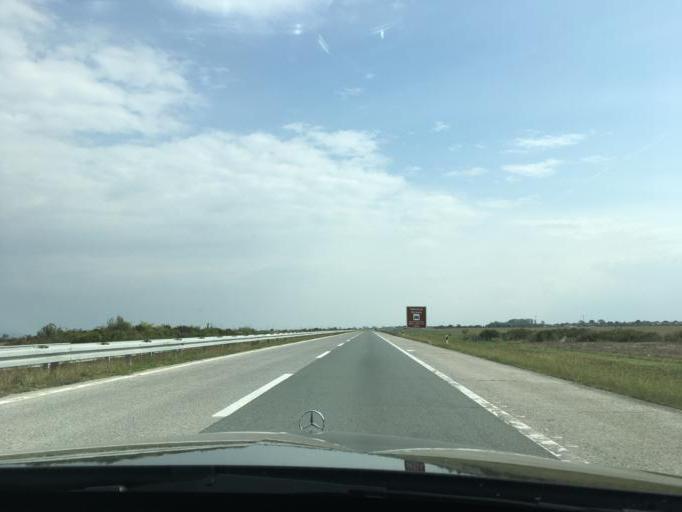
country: RS
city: Macvanska Mitrovica
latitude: 45.0174
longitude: 19.5449
